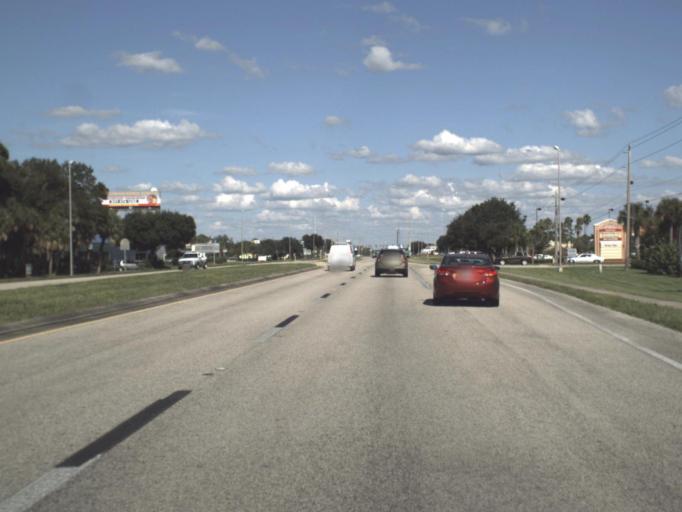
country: US
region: Florida
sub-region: Charlotte County
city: Port Charlotte
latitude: 27.0107
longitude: -82.1524
